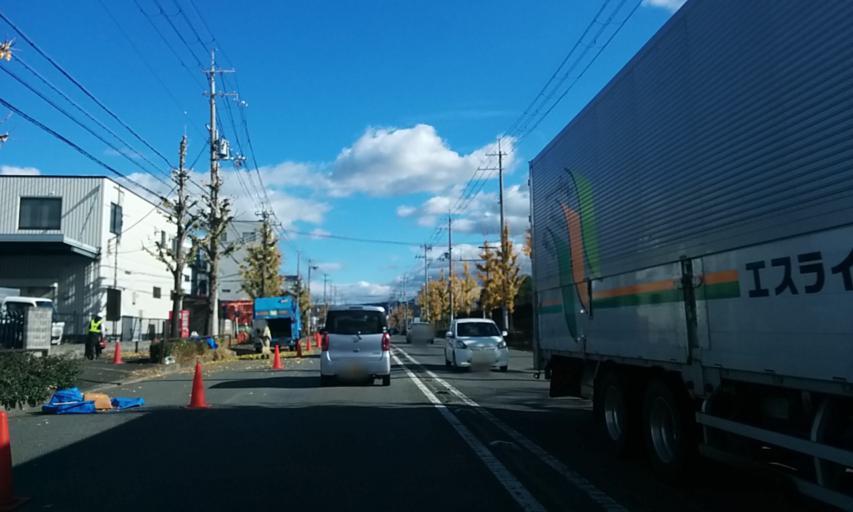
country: JP
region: Kyoto
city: Muko
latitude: 34.9605
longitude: 135.7352
